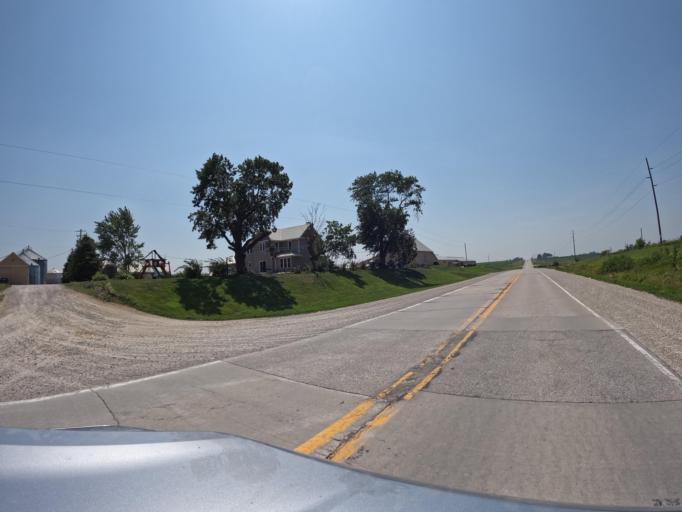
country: US
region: Iowa
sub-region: Keokuk County
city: Sigourney
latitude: 41.3368
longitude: -92.2516
